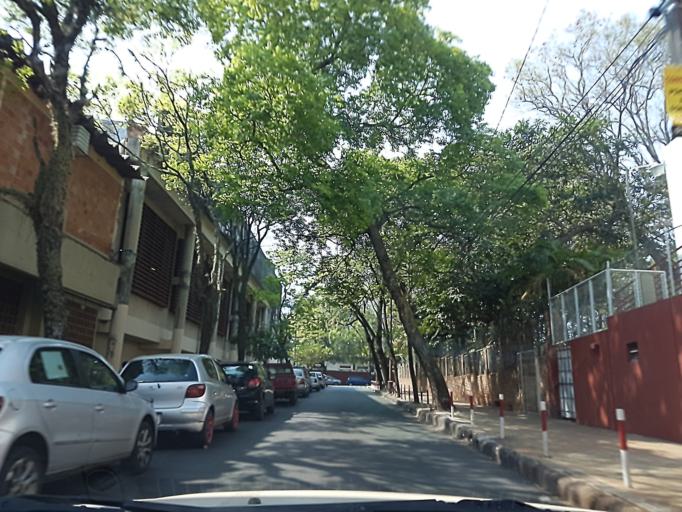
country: PY
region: Asuncion
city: Asuncion
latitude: -25.2892
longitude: -57.6164
